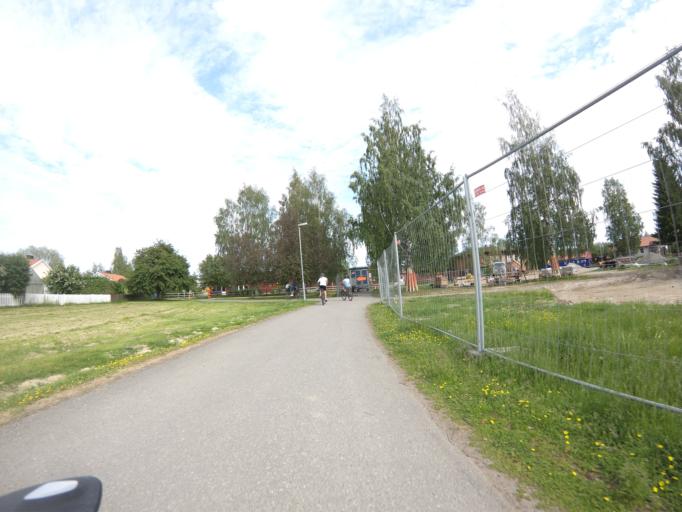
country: SE
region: Vaesterbotten
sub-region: Umea Kommun
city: Umea
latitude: 63.8169
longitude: 20.2605
